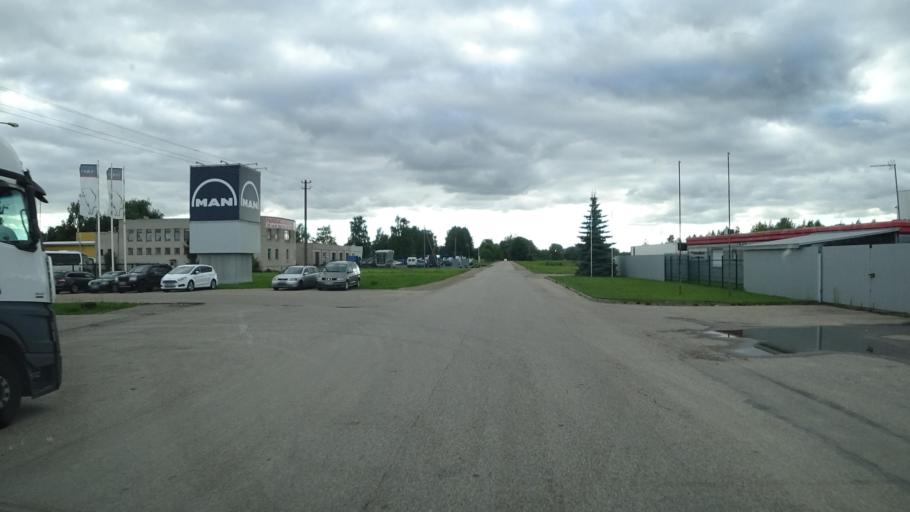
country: LT
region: Marijampoles apskritis
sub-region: Marijampole Municipality
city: Marijampole
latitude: 54.5814
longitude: 23.3734
